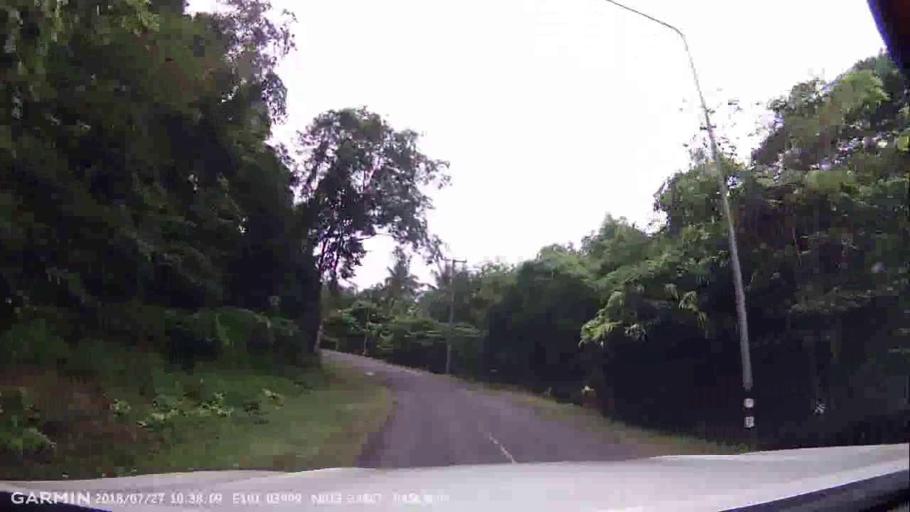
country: TH
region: Chon Buri
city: Ban Bueng
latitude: 13.2381
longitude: 101.0400
